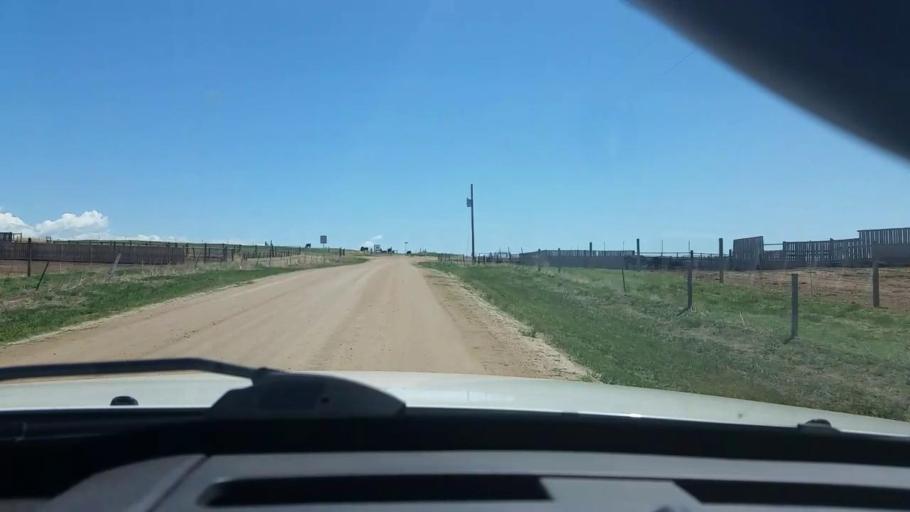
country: US
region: Colorado
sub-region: Larimer County
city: Wellington
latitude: 40.7982
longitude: -105.0407
